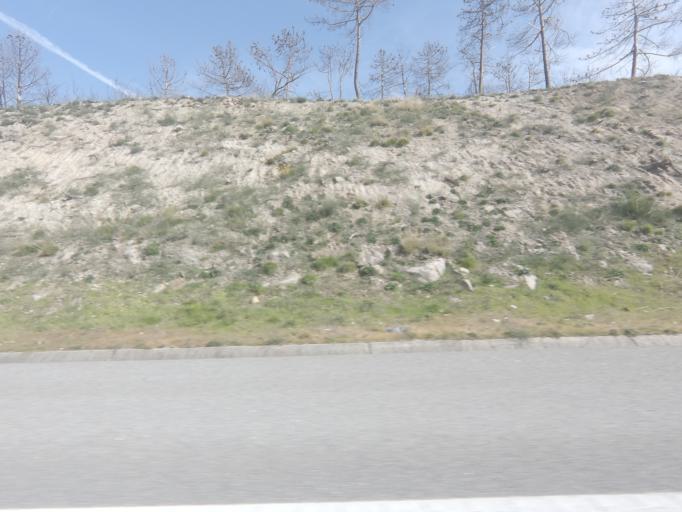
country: PT
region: Viseu
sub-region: Vouzela
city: Vouzela
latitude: 40.7016
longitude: -8.1133
